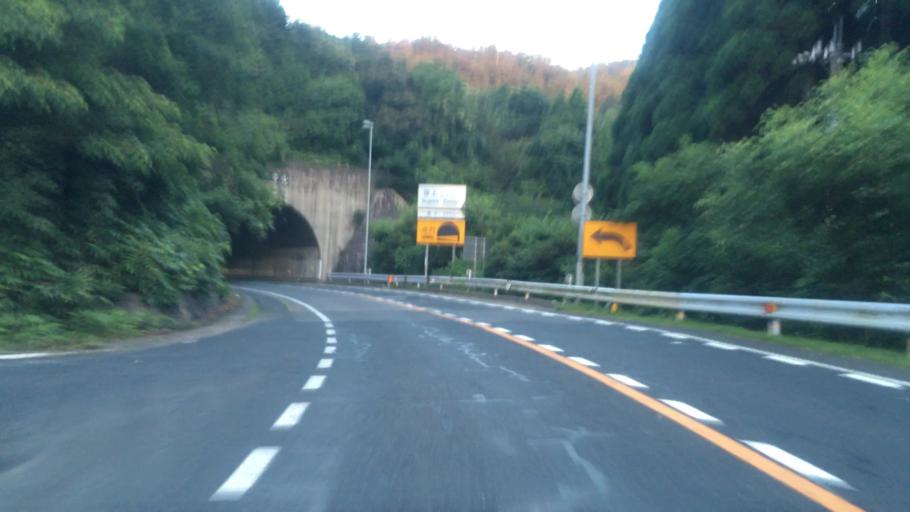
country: JP
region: Tottori
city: Tottori
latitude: 35.5943
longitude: 134.3542
